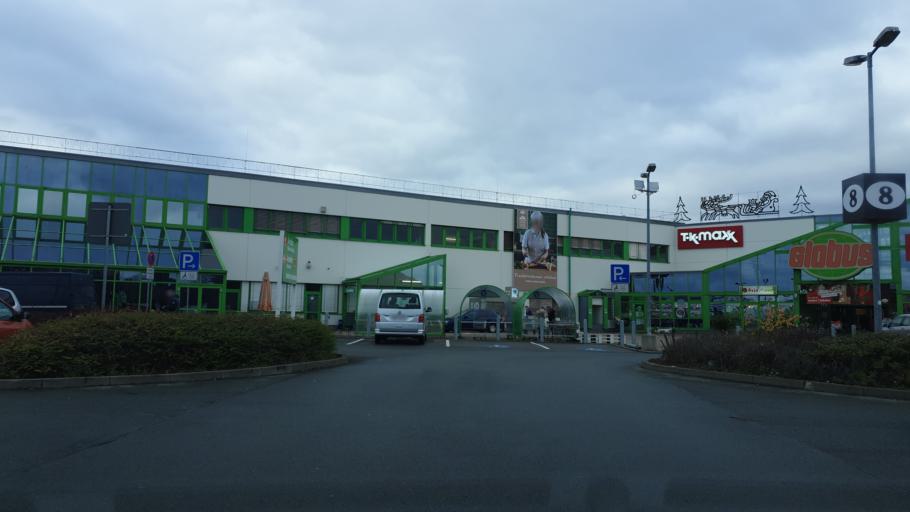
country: DE
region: Saxony
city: Zwickau
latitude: 50.7066
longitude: 12.4970
